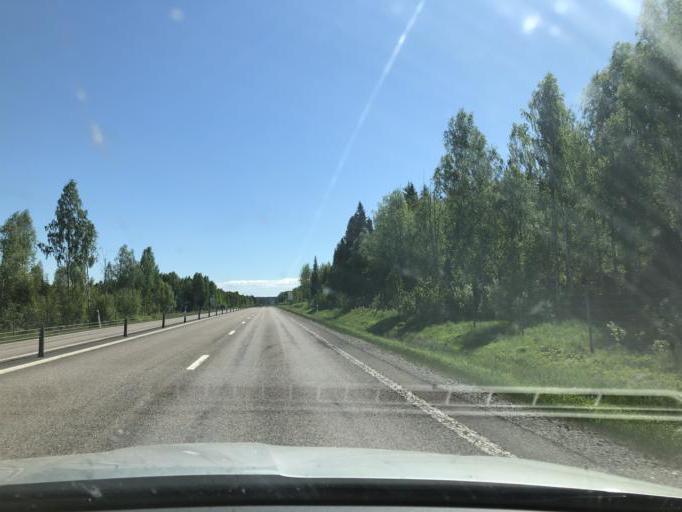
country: SE
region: Norrbotten
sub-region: Kalix Kommun
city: Toere
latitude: 65.8982
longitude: 22.8766
